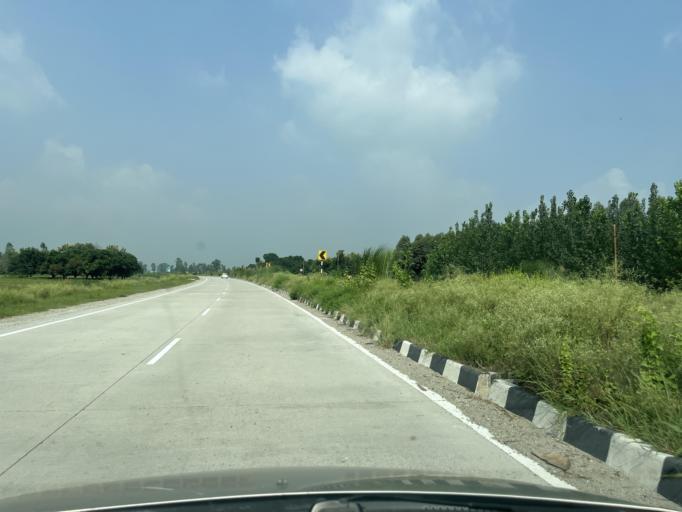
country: IN
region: Uttarakhand
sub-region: Udham Singh Nagar
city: Kashipur
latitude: 29.1663
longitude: 78.9856
